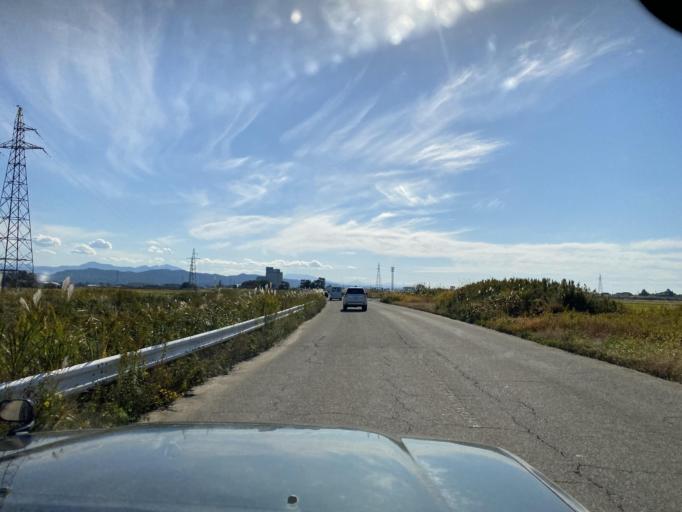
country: JP
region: Niigata
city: Niitsu-honcho
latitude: 37.8006
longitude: 139.0767
